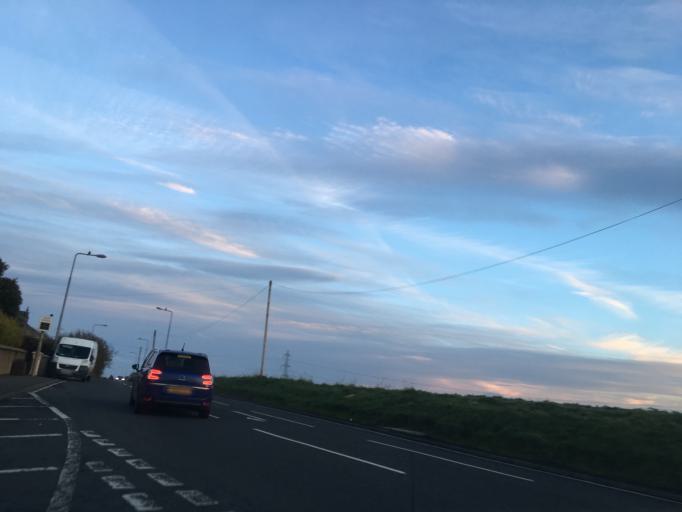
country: GB
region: Scotland
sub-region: Fife
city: Cairneyhill
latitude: 56.0845
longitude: -3.5259
